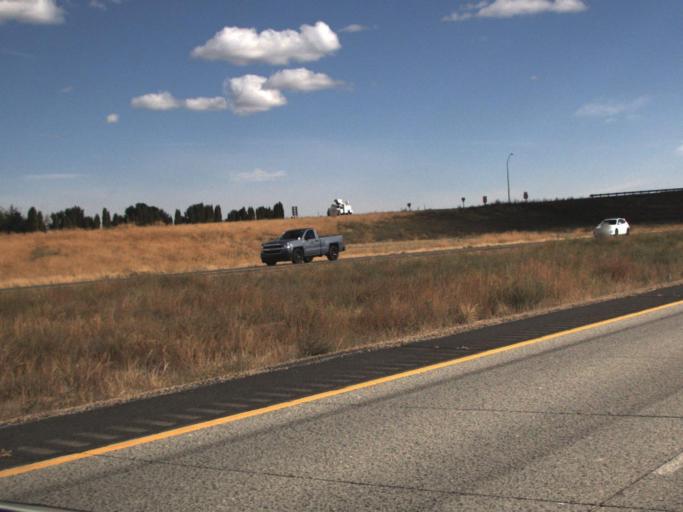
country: US
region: Washington
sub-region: Yakima County
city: Grandview
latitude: 46.2566
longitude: -119.8807
